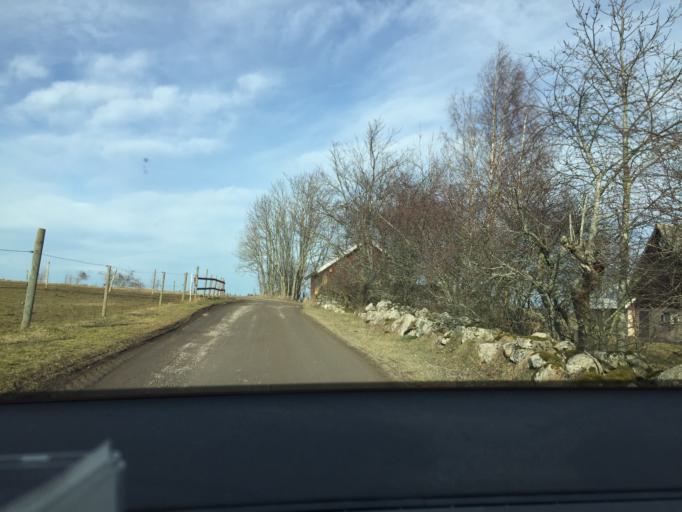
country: SE
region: OErebro
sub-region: Hallsbergs Kommun
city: Skollersta
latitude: 59.1351
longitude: 15.4120
